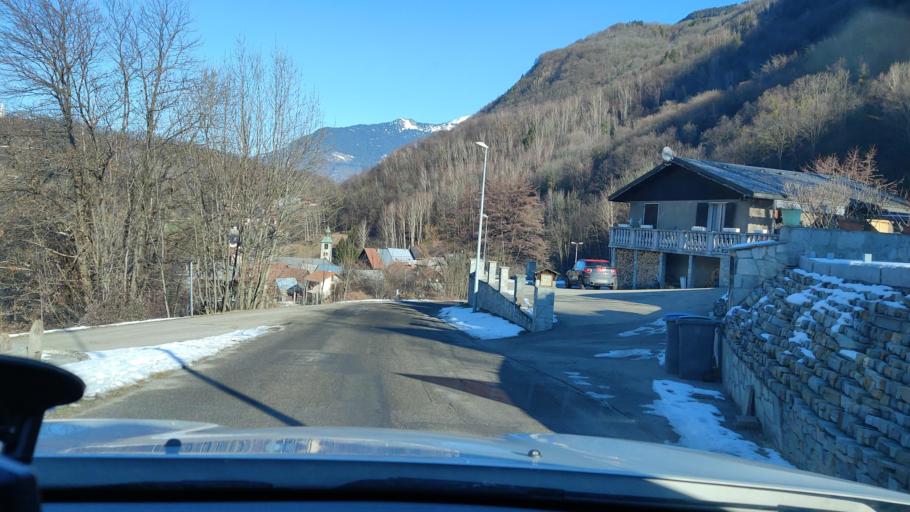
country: FR
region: Rhone-Alpes
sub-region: Departement de la Savoie
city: La Bathie
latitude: 45.5894
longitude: 6.4579
